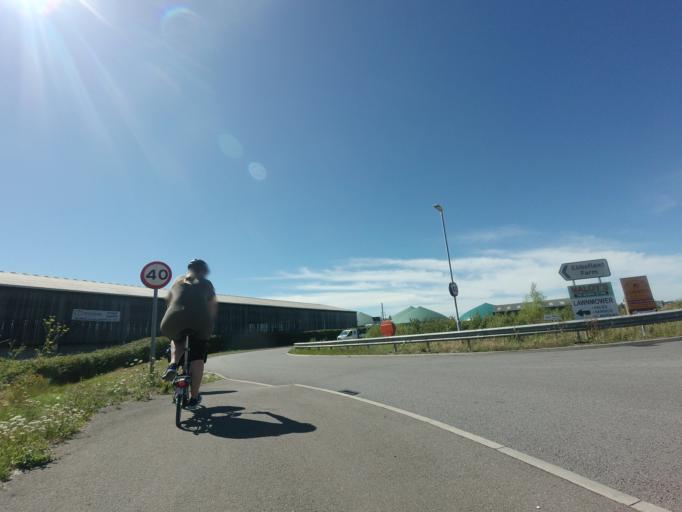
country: GB
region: England
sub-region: Kent
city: Sandwich
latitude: 51.3118
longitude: 1.3500
